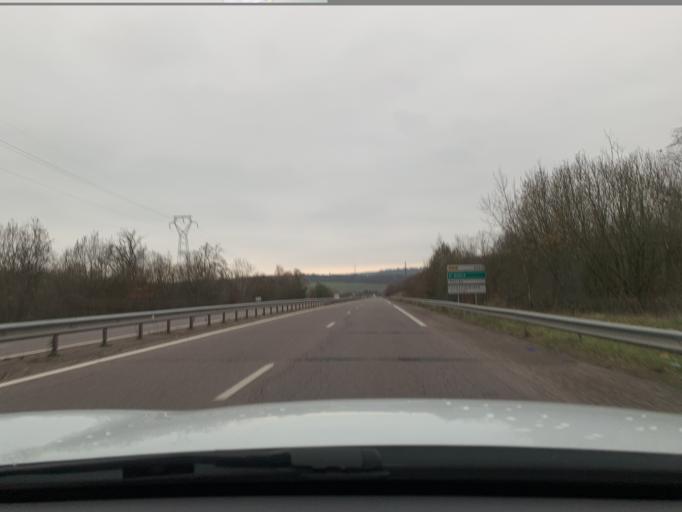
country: FR
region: Lorraine
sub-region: Departement de la Moselle
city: Woustviller
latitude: 49.1010
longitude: 7.0309
